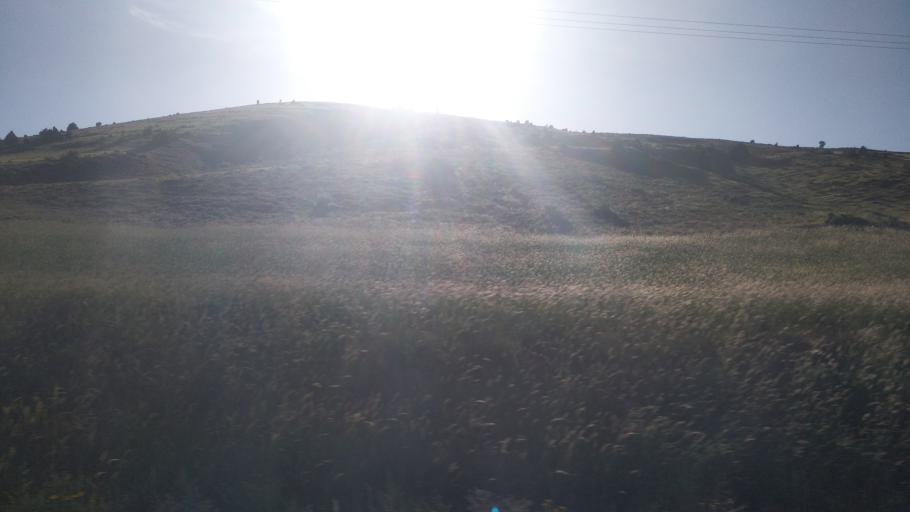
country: TR
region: Bitlis
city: Resadiye
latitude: 38.4753
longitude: 42.5494
